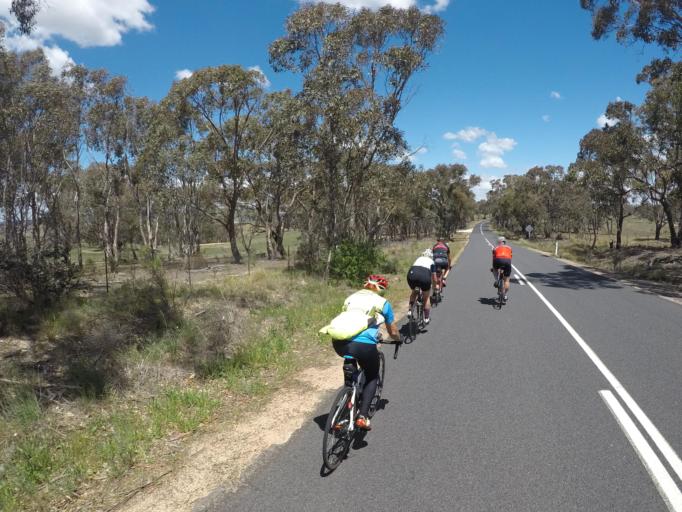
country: AU
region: New South Wales
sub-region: Bathurst Regional
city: Perthville
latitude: -33.5309
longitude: 149.4479
